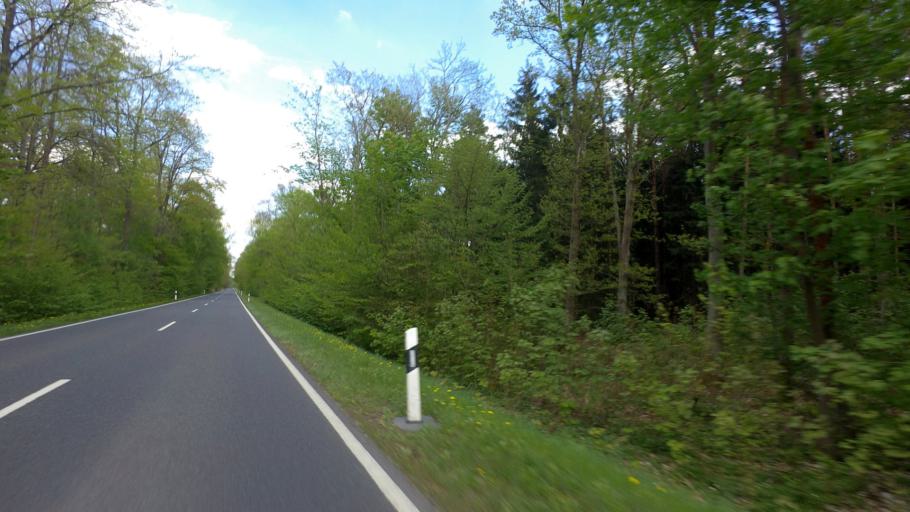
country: DE
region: Brandenburg
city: Wandlitz
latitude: 52.8274
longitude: 13.5014
